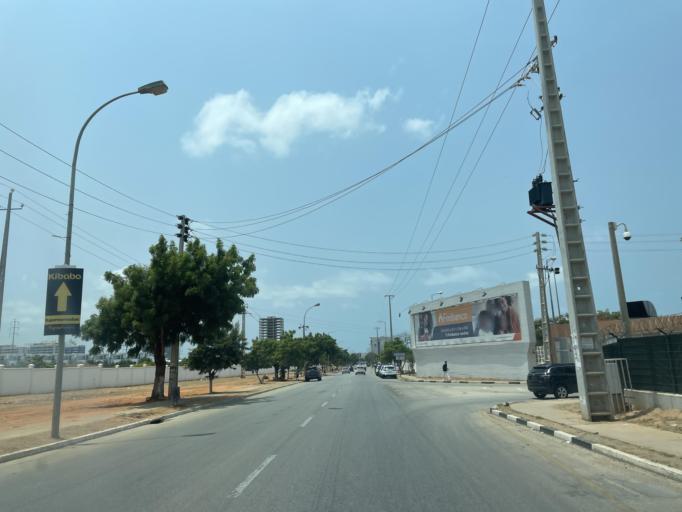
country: AO
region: Luanda
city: Luanda
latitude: -8.9153
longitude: 13.1924
